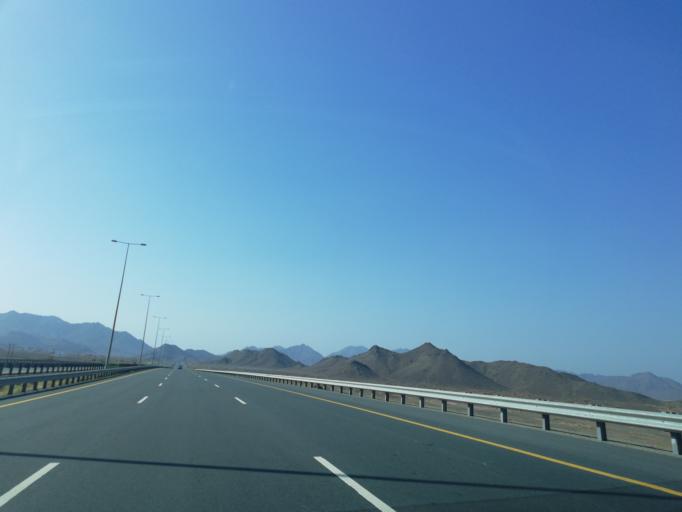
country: OM
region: Ash Sharqiyah
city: Ibra'
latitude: 22.9391
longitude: 58.2504
